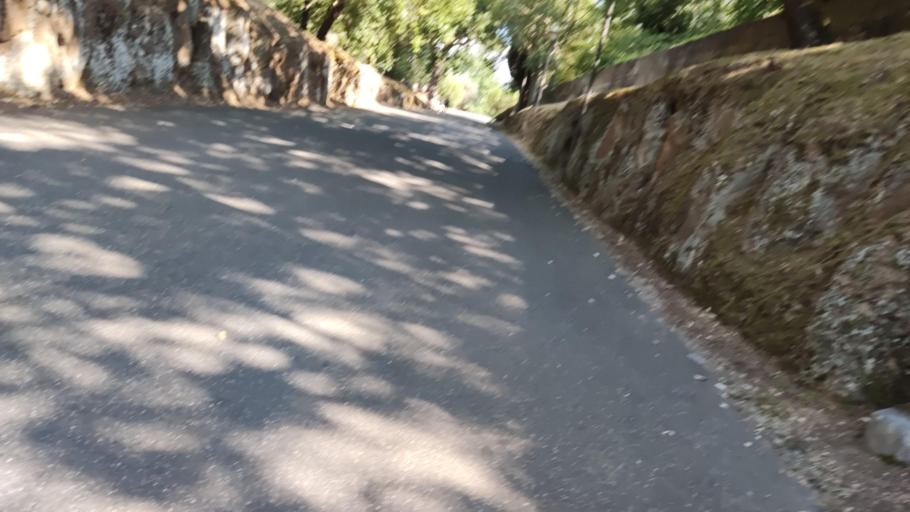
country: IT
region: Latium
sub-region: Citta metropolitana di Roma Capitale
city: Villa Adriana
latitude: 41.9441
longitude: 12.7729
